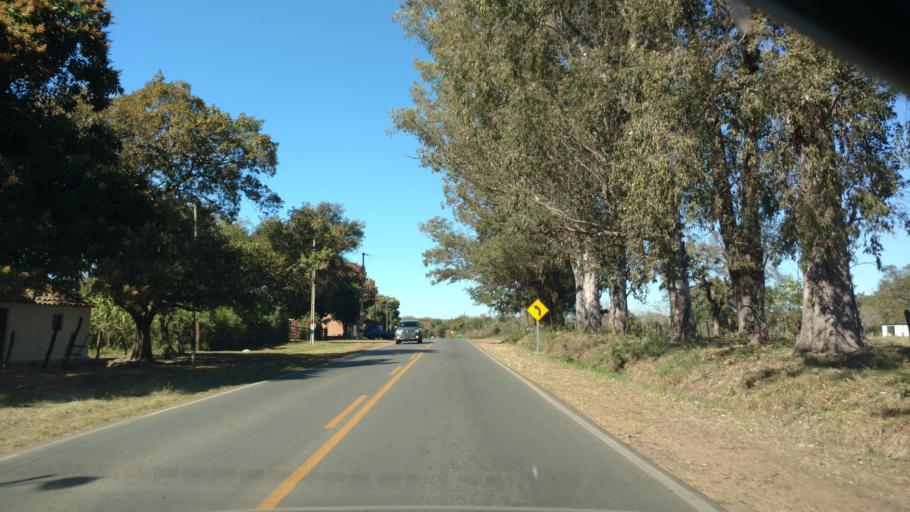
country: PY
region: Central
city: Ypacarai
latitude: -25.4438
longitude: -57.2764
